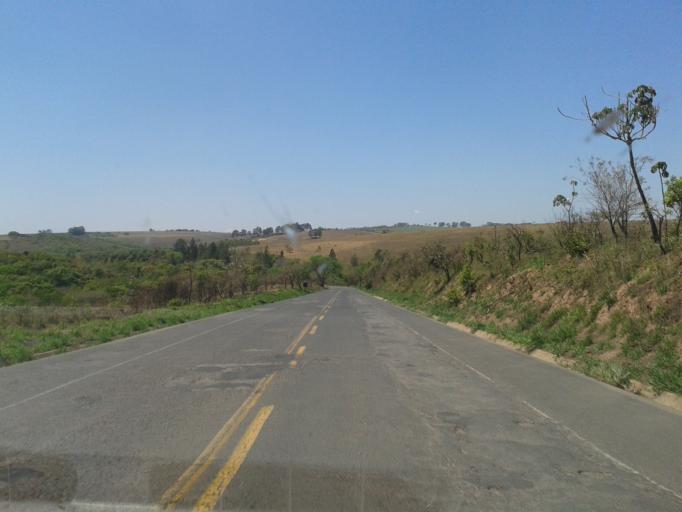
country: BR
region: Minas Gerais
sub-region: Araxa
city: Araxa
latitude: -19.4506
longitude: -47.1870
